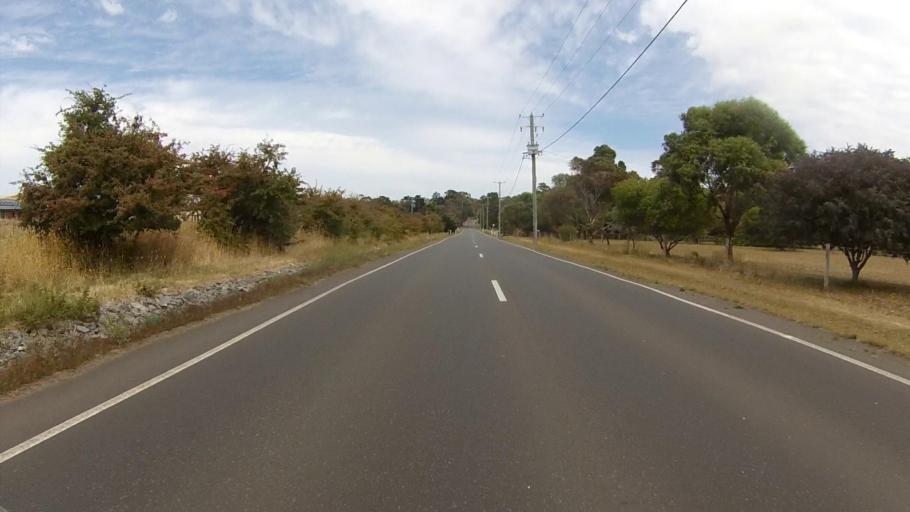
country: AU
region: Tasmania
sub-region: Clarence
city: Seven Mile Beach
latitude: -42.8639
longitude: 147.4908
